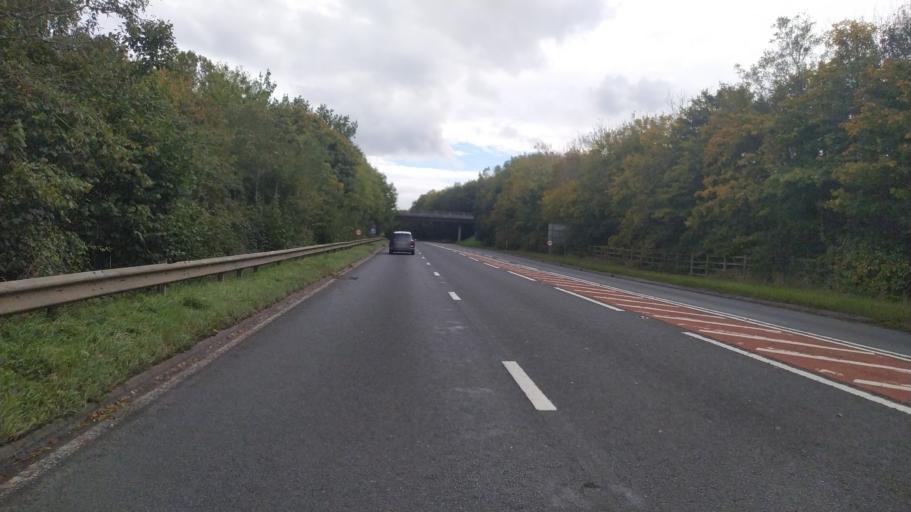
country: GB
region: England
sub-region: Dorset
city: Bridport
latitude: 50.7276
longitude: -2.7778
